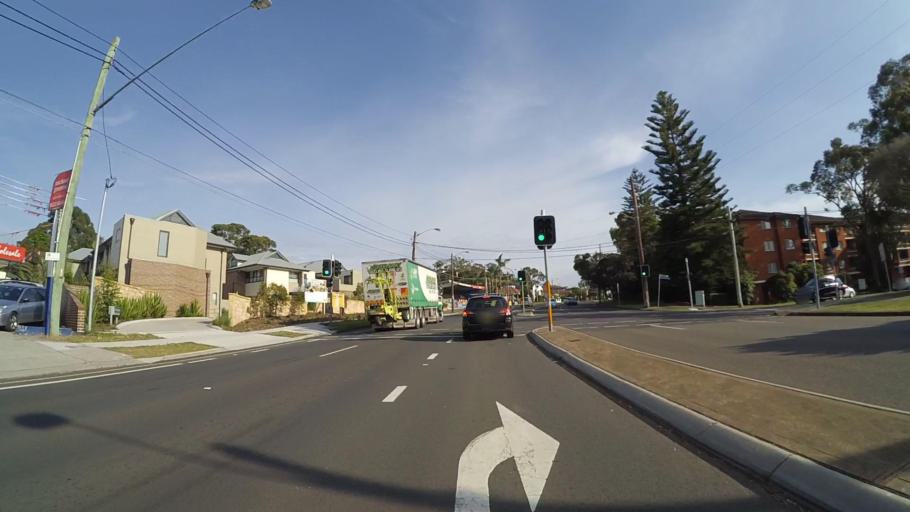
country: AU
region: New South Wales
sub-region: Sutherland Shire
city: Kareela
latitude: -34.0143
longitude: 151.1047
